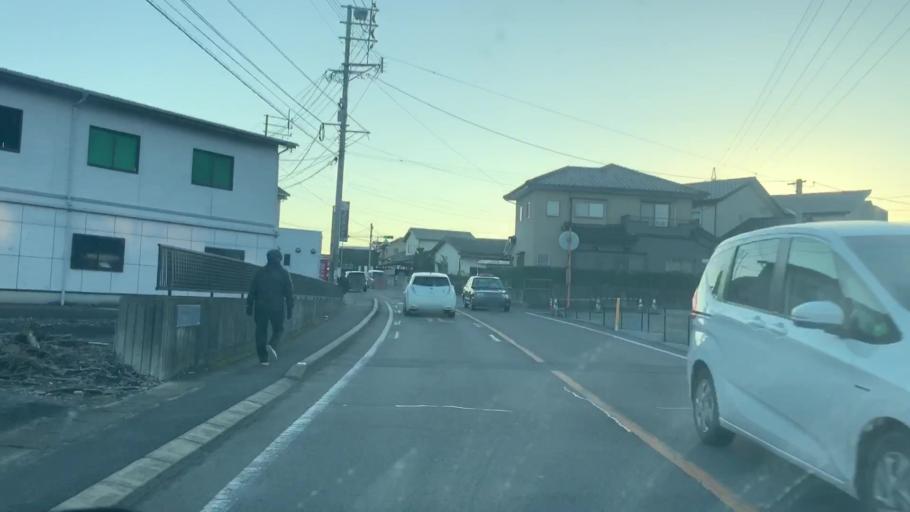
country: JP
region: Saga Prefecture
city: Takeocho-takeo
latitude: 33.2081
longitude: 130.0273
